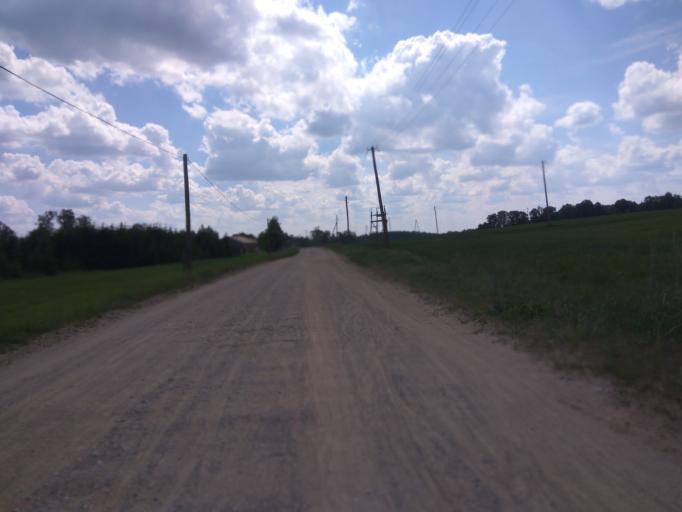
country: LV
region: Kuldigas Rajons
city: Kuldiga
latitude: 56.8961
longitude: 21.9688
